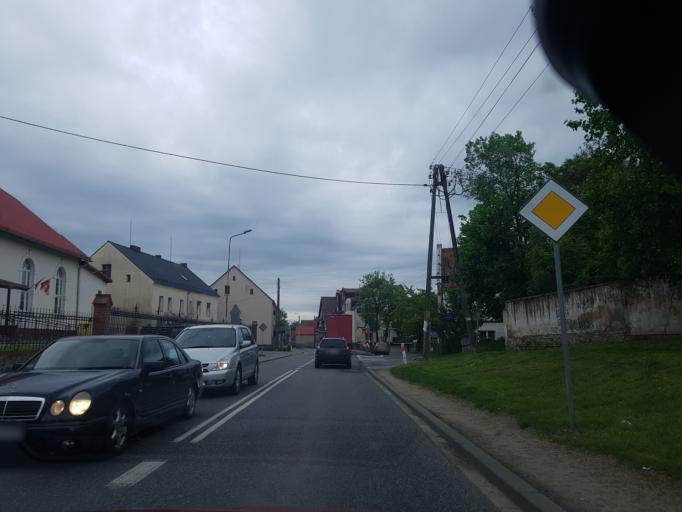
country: PL
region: Lower Silesian Voivodeship
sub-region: Powiat wroclawski
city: Gniechowice
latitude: 50.9870
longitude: 16.8345
